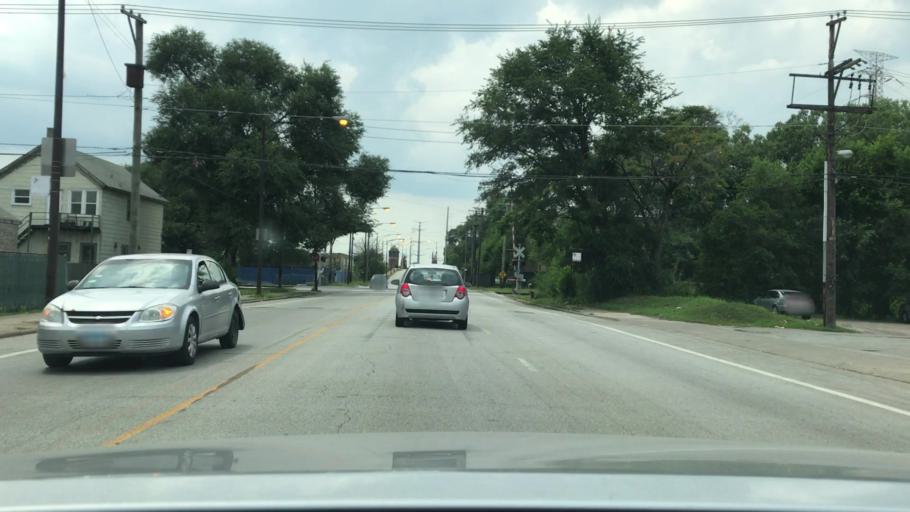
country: US
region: Indiana
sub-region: Lake County
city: Whiting
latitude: 41.7139
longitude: -87.5379
